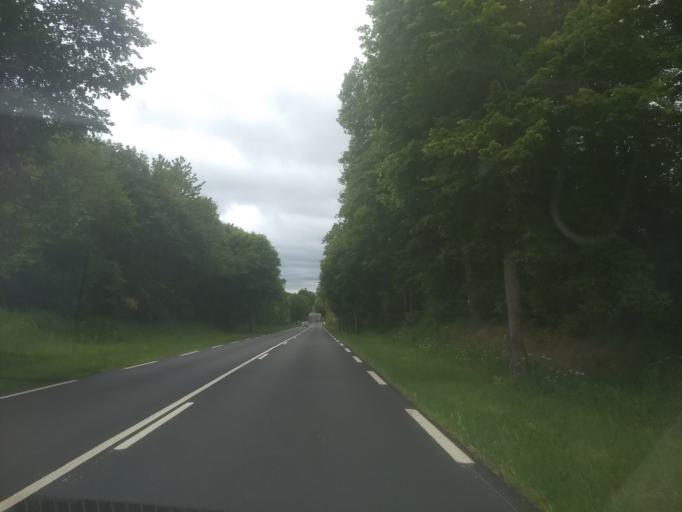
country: FR
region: Centre
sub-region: Departement d'Eure-et-Loir
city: Treon
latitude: 48.6488
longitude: 1.2898
